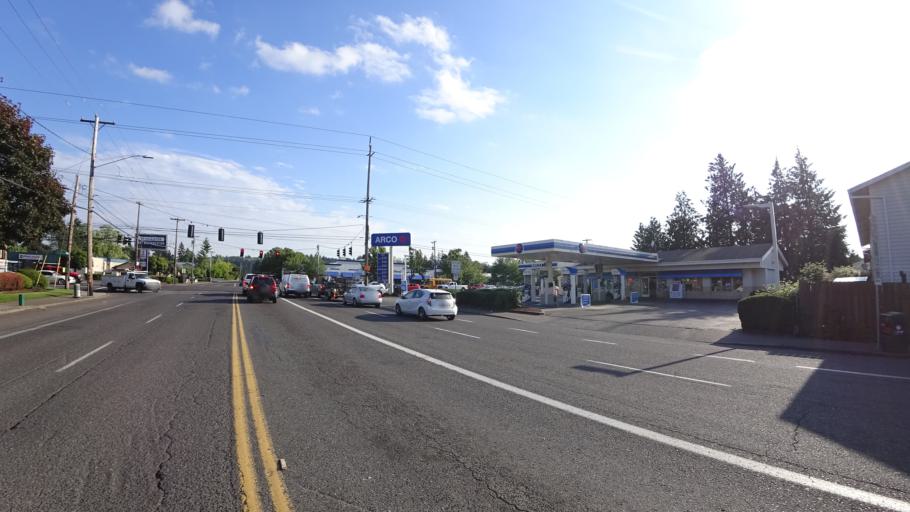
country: US
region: Oregon
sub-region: Multnomah County
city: Gresham
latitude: 45.5051
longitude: -122.4966
